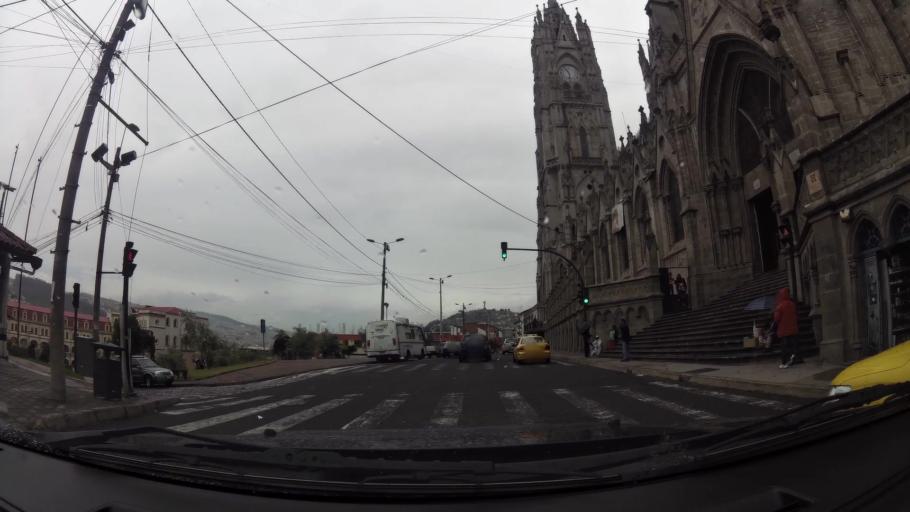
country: EC
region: Pichincha
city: Quito
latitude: -0.2147
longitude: -78.5069
